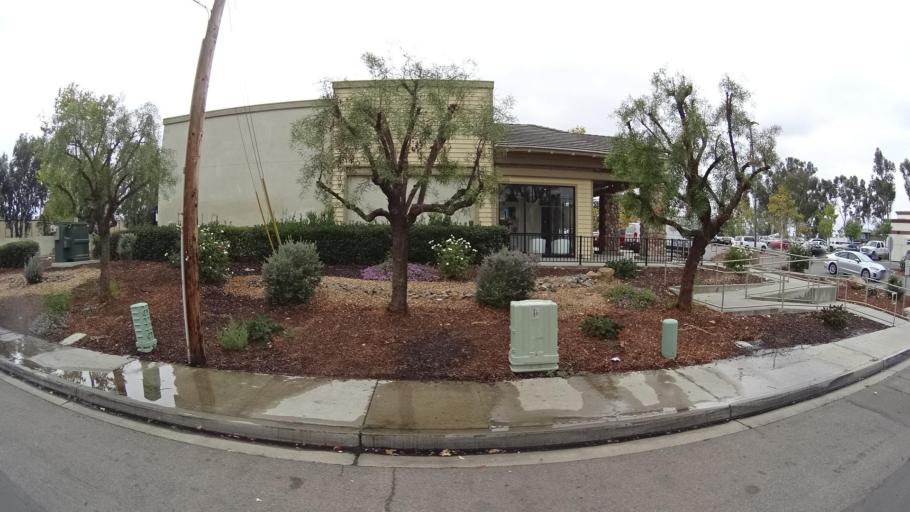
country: US
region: California
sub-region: San Diego County
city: Ramona
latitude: 33.0360
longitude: -116.8775
